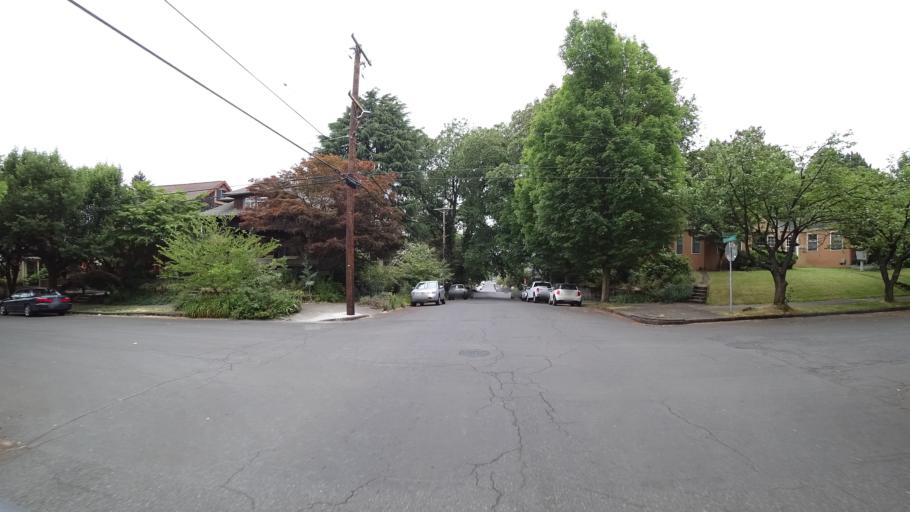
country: US
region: Oregon
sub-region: Multnomah County
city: Portland
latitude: 45.4997
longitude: -122.6579
